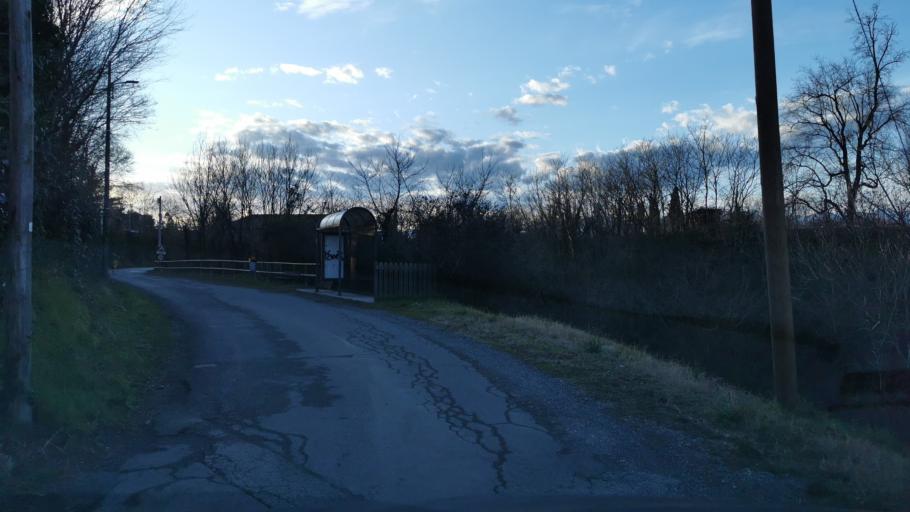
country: IT
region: Piedmont
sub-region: Provincia di Torino
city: Rivarossa
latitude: 45.2519
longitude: 7.7113
